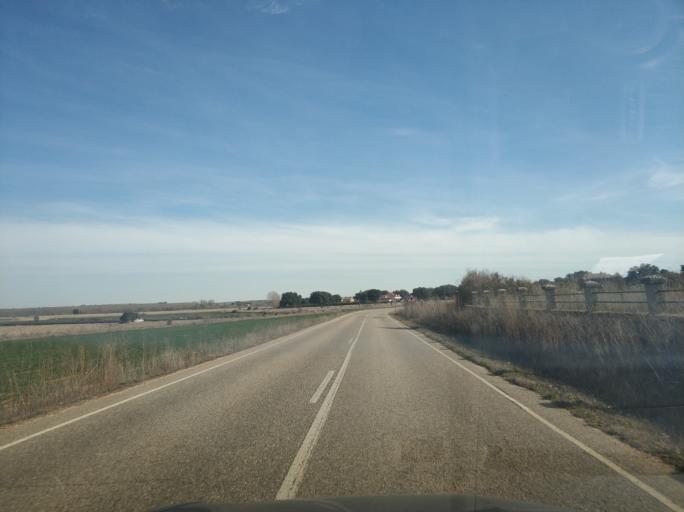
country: ES
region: Castille and Leon
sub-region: Provincia de Salamanca
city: Florida de Liebana
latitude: 41.0228
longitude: -5.7499
